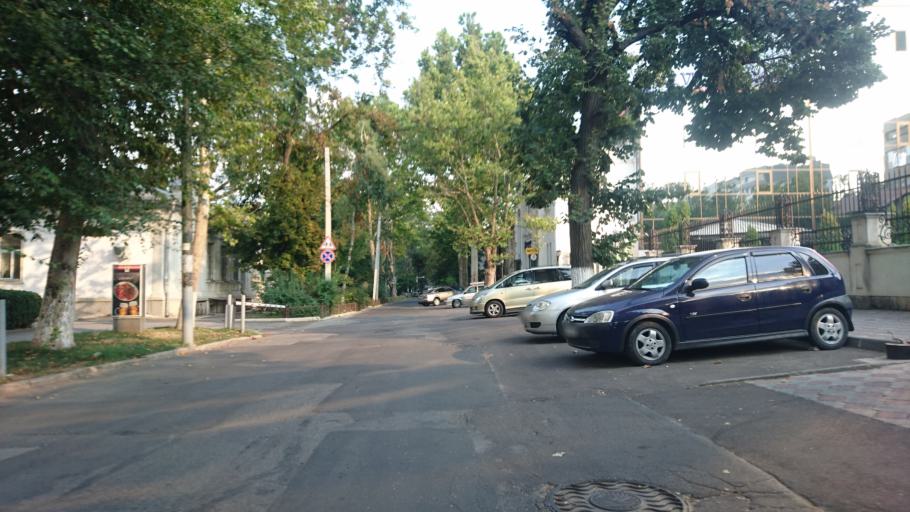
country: MD
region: Chisinau
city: Chisinau
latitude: 47.0286
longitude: 28.8207
